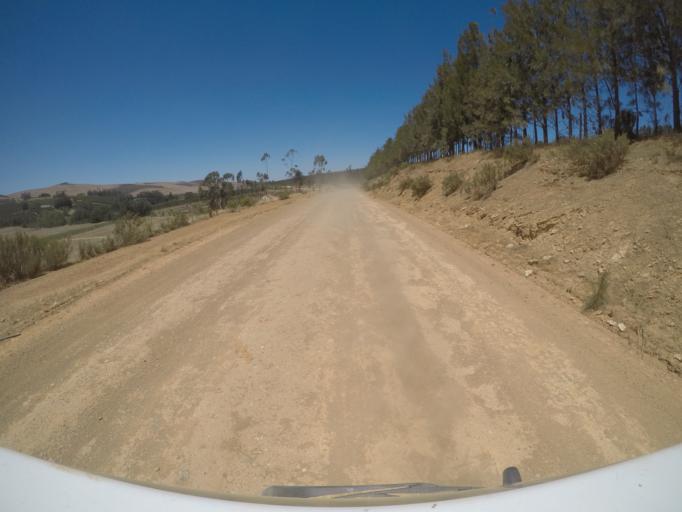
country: ZA
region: Western Cape
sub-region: Overberg District Municipality
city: Grabouw
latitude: -34.0898
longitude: 19.1912
